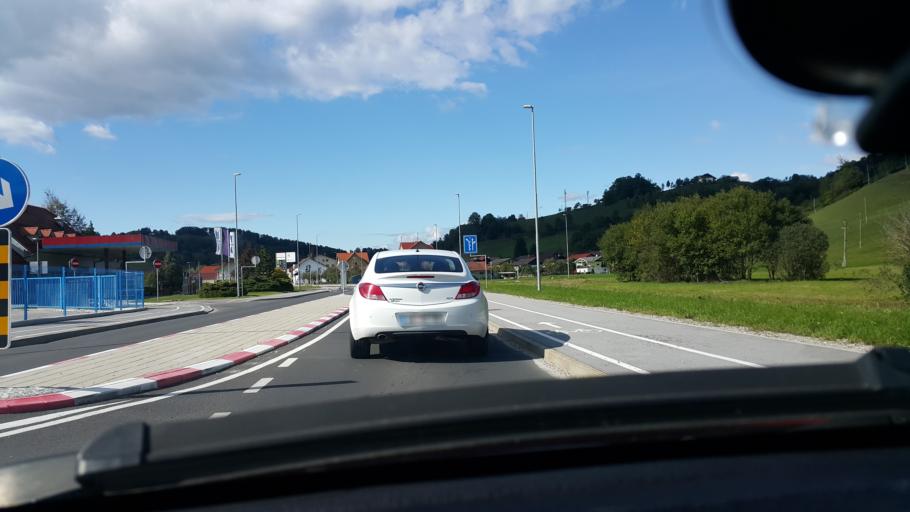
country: SI
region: Kungota
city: Zgornja Kungota
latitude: 46.6346
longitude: 15.6209
